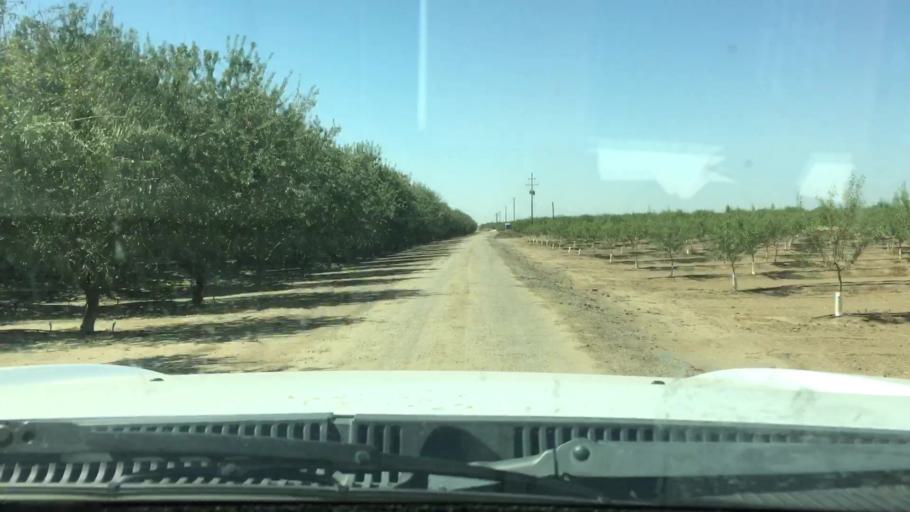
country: US
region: California
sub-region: Kern County
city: Shafter
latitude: 35.4563
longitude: -119.2993
